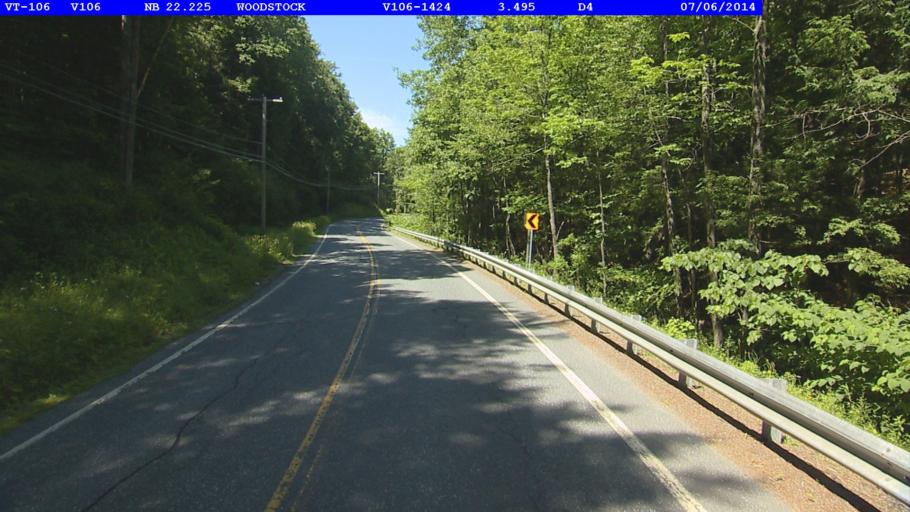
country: US
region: Vermont
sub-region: Windsor County
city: Woodstock
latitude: 43.5718
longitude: -72.5163
